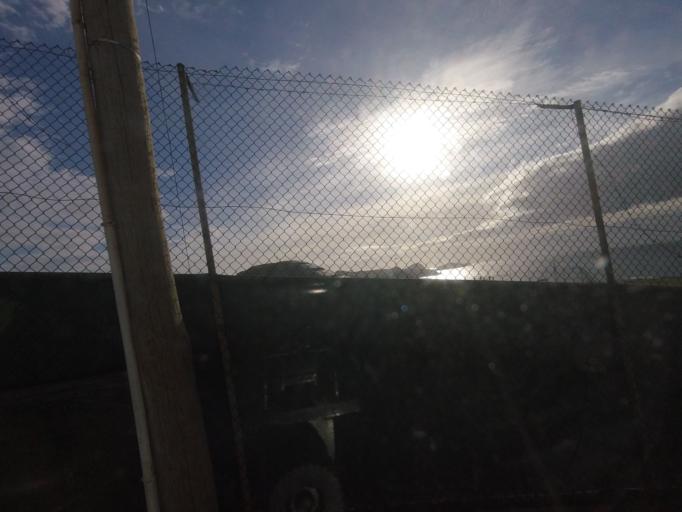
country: PT
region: Madeira
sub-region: Machico
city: Canical
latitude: 32.7429
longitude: -16.7379
